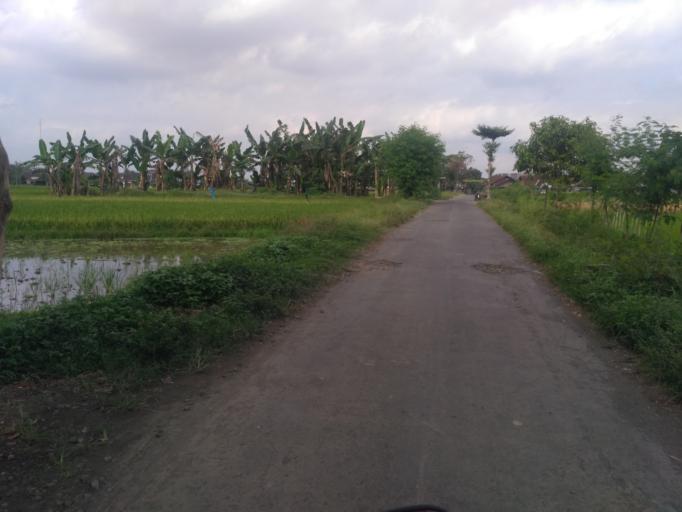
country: ID
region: Daerah Istimewa Yogyakarta
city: Yogyakarta
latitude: -7.7601
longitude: 110.3543
